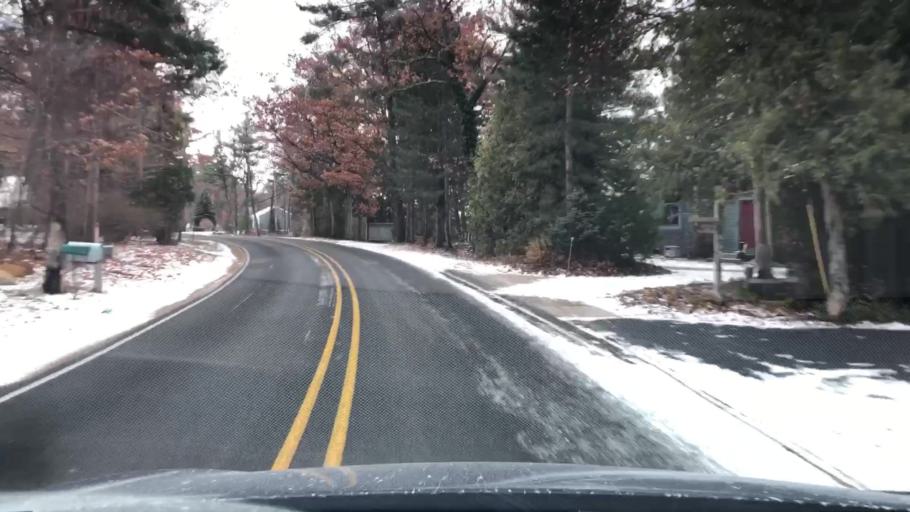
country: US
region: Michigan
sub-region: Grand Traverse County
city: Traverse City
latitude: 44.8170
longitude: -85.5787
